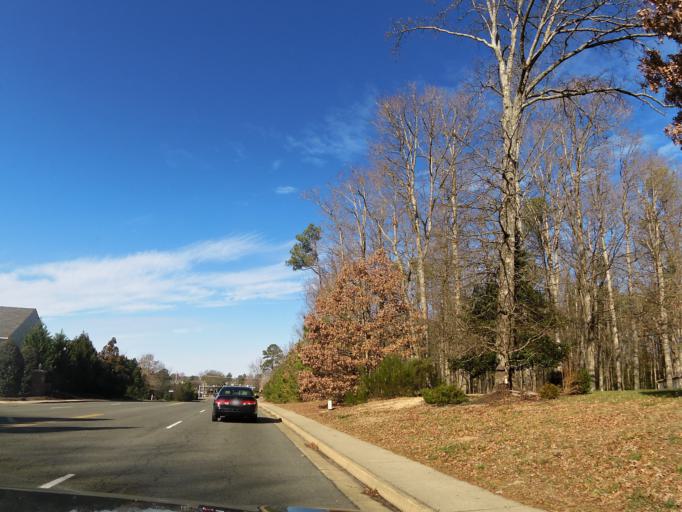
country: US
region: Virginia
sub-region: Henrico County
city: Tuckahoe
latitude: 37.6366
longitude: -77.5616
